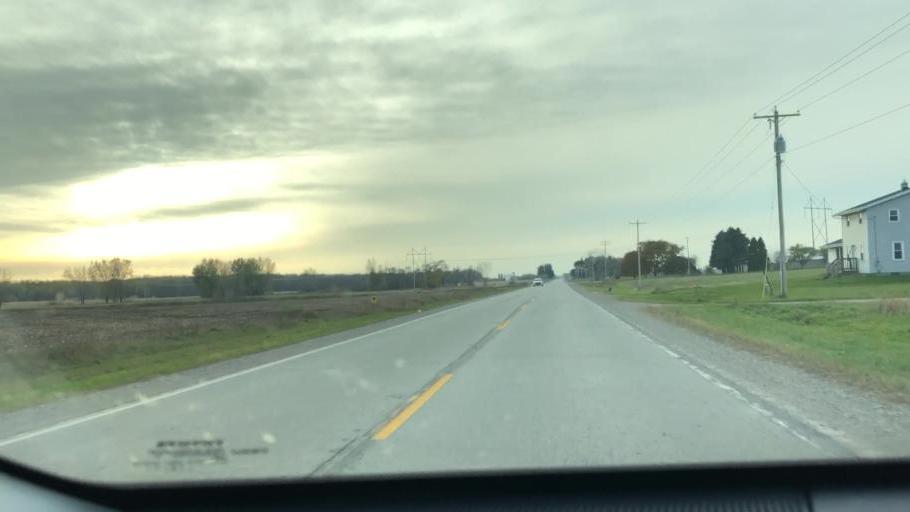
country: US
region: Wisconsin
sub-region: Outagamie County
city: Seymour
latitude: 44.4437
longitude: -88.3086
